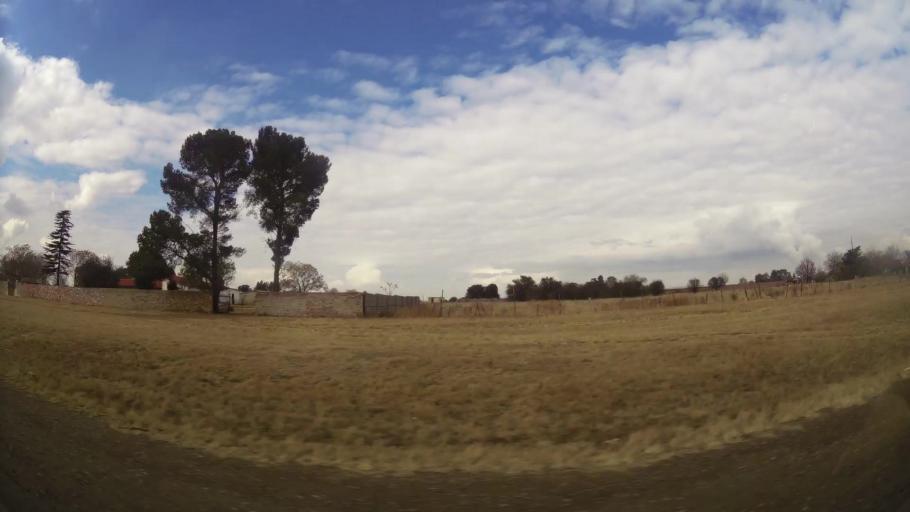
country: ZA
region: Gauteng
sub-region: Sedibeng District Municipality
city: Meyerton
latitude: -26.6467
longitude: 28.0259
